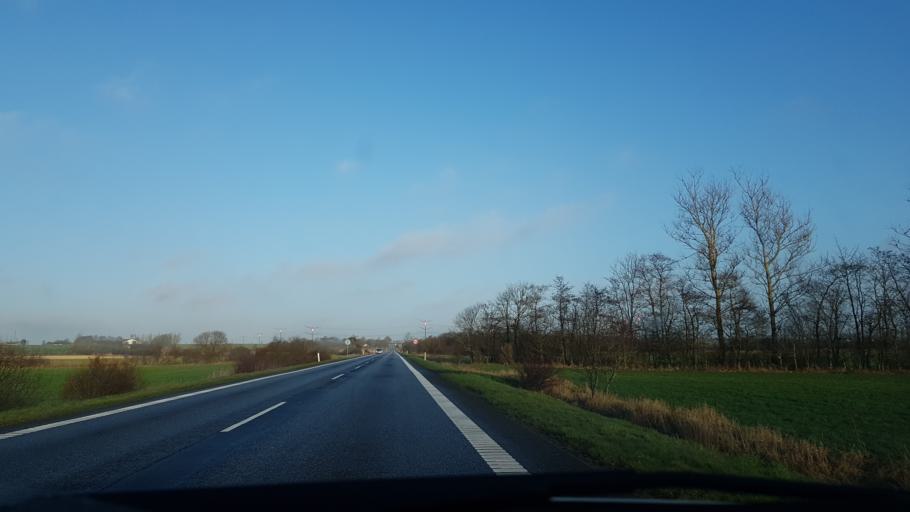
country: DK
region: South Denmark
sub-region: Tonder Kommune
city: Toftlund
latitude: 55.2415
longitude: 9.1315
